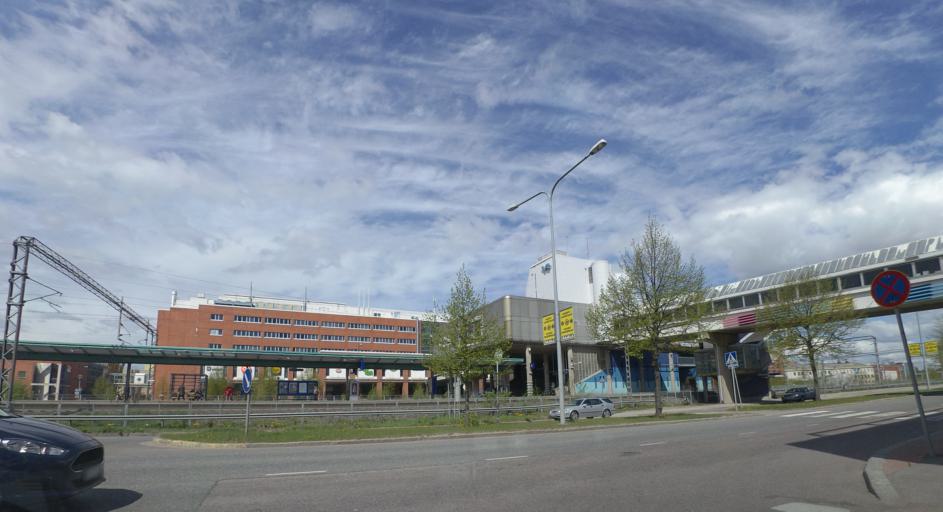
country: FI
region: Uusimaa
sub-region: Helsinki
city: Vantaa
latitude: 60.2508
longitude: 25.0117
